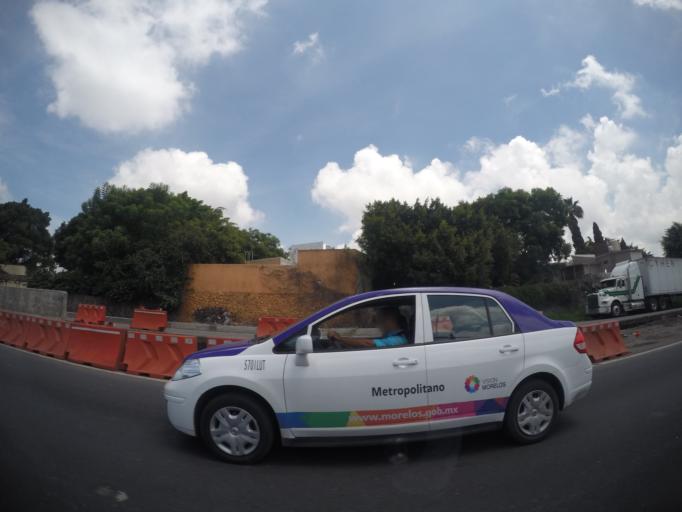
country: MX
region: Morelos
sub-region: Cuernavaca
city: Colonia los Cerritos
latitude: 18.9342
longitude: -99.1982
